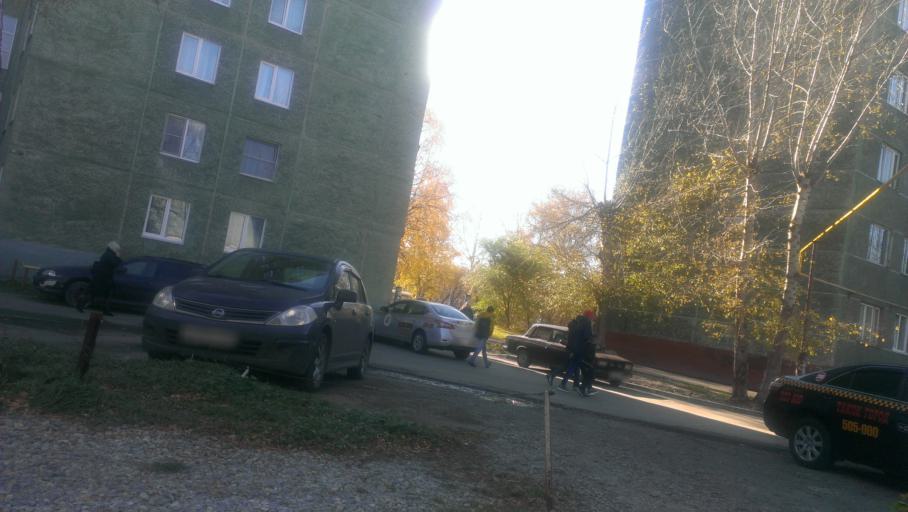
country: RU
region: Altai Krai
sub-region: Gorod Barnaulskiy
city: Barnaul
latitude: 53.3619
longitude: 83.6849
